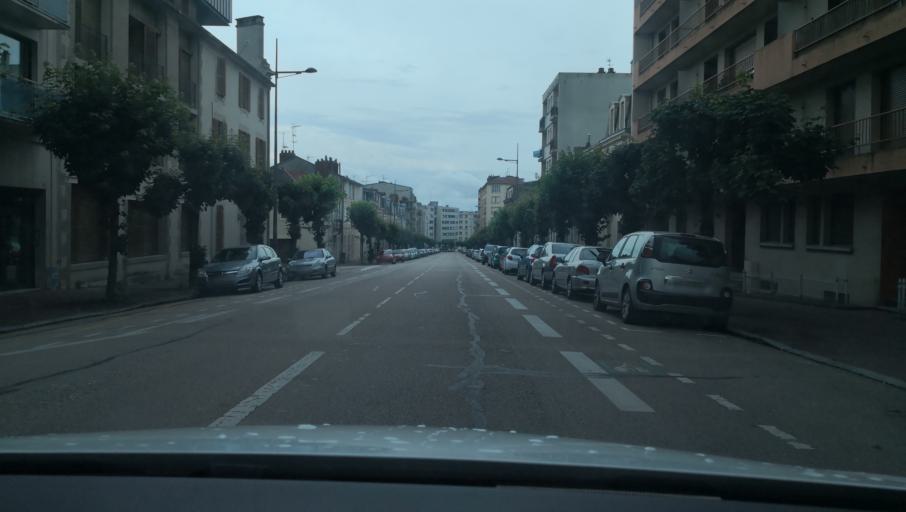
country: FR
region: Limousin
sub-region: Departement de la Haute-Vienne
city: Limoges
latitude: 45.8389
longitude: 1.2614
